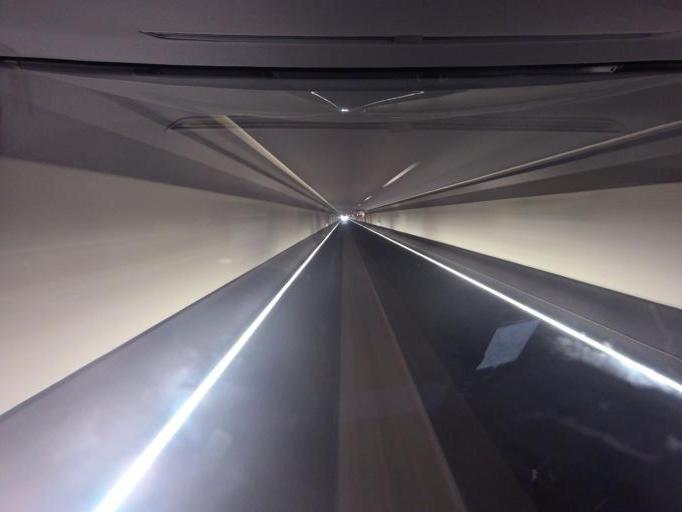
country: NL
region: North Holland
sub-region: Gemeente Velsen
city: Velsen-Zuid
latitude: 52.4645
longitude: 4.6539
